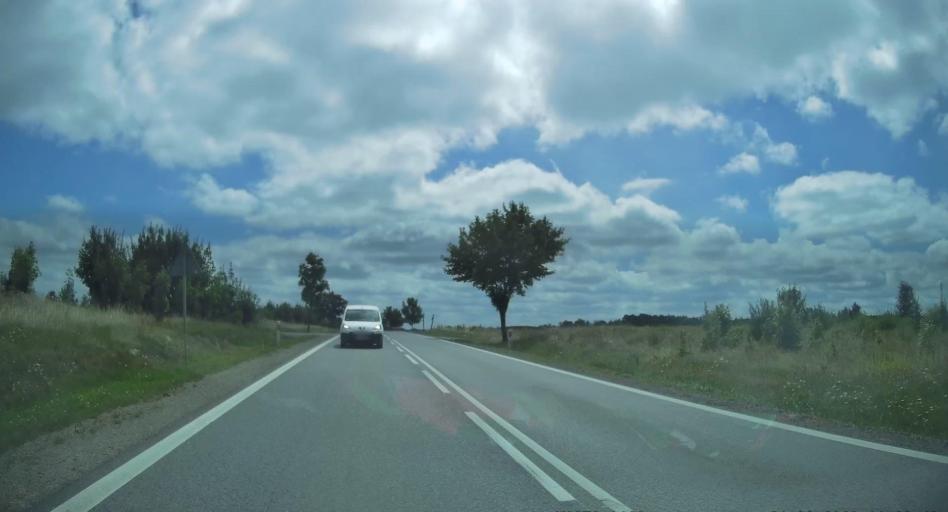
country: PL
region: Swietokrzyskie
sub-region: Powiat sandomierski
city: Klimontow
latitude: 50.6476
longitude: 21.4588
